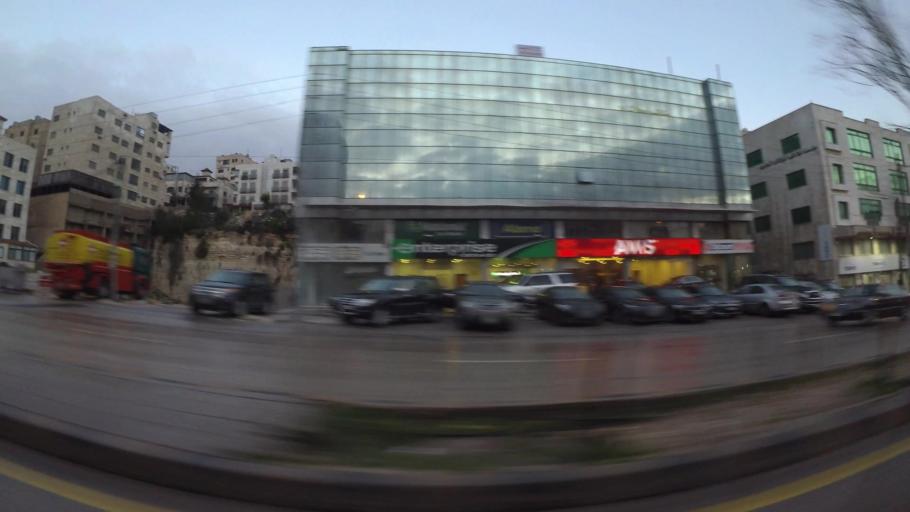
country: JO
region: Amman
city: Al Jubayhah
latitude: 31.9730
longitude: 35.8866
